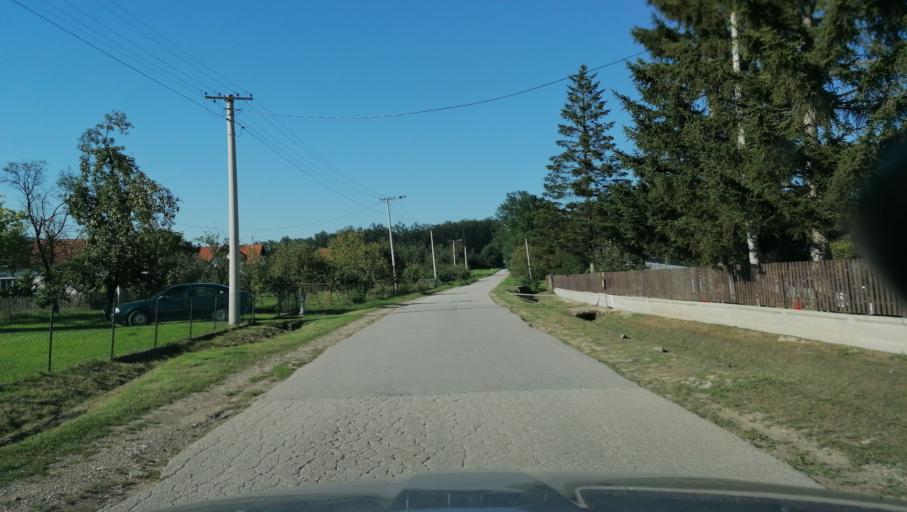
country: RS
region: Central Serbia
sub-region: Sumadijski Okrug
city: Knic
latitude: 43.8812
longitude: 20.6134
